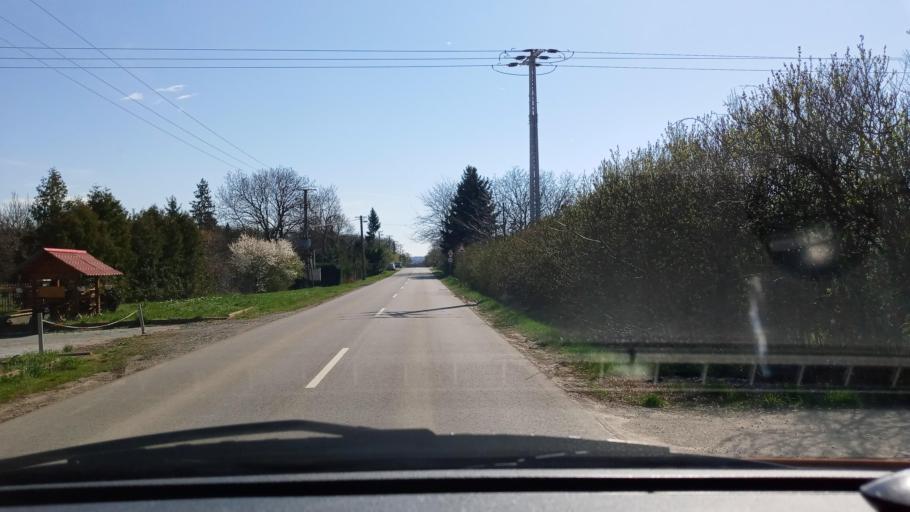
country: HU
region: Baranya
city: Kozarmisleny
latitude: 46.0859
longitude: 18.2978
